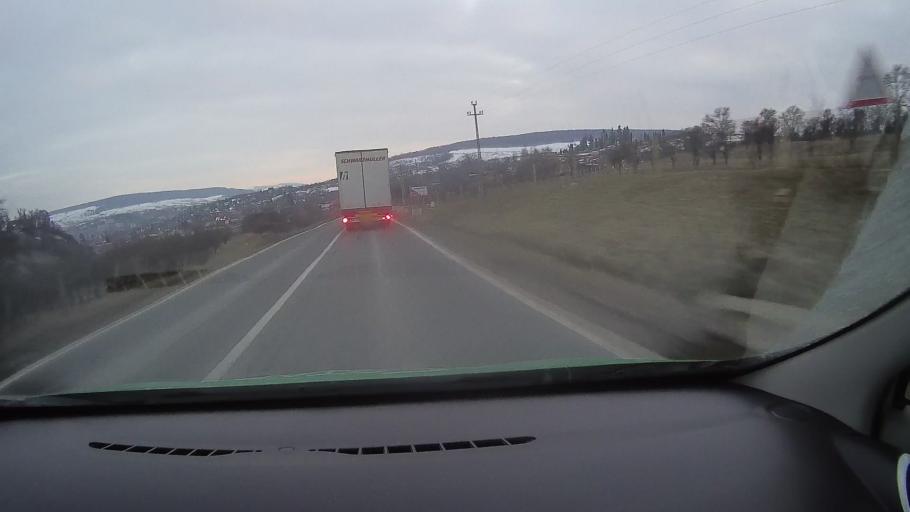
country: RO
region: Harghita
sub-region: Municipiul Odorheiu Secuiesc
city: Odorheiu Secuiesc
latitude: 46.3217
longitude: 25.2801
